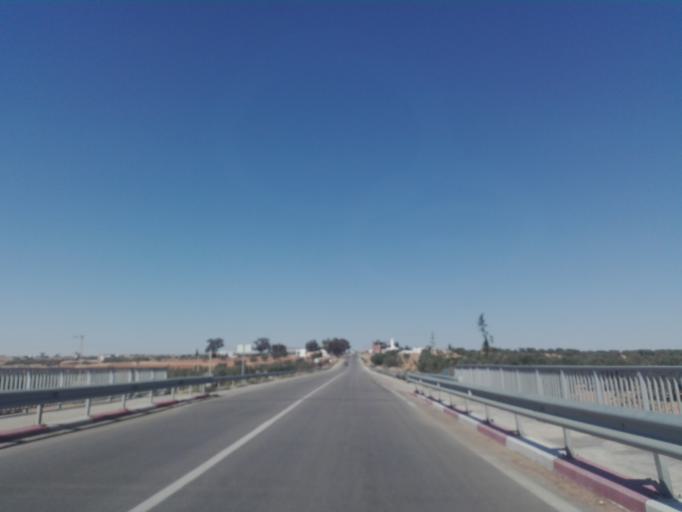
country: TN
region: Safaqis
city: Bi'r `Ali Bin Khalifah
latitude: 34.7412
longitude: 10.3773
